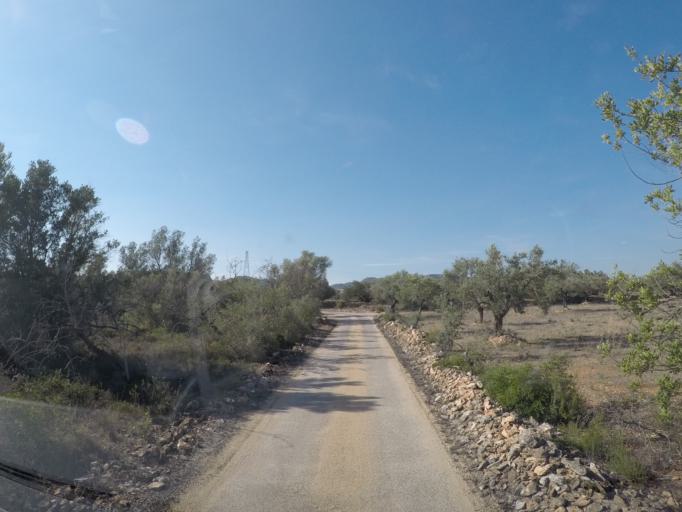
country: ES
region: Catalonia
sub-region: Provincia de Tarragona
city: El Perello
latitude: 40.9012
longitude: 0.7303
